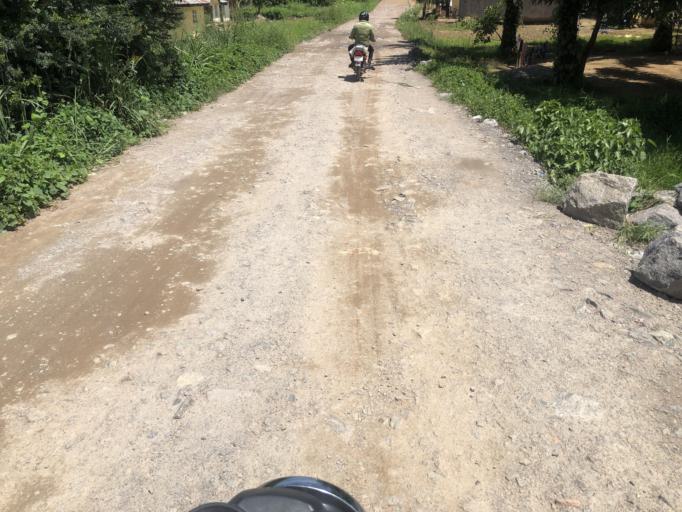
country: SL
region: Eastern Province
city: Koidu
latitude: 8.6447
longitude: -10.9580
